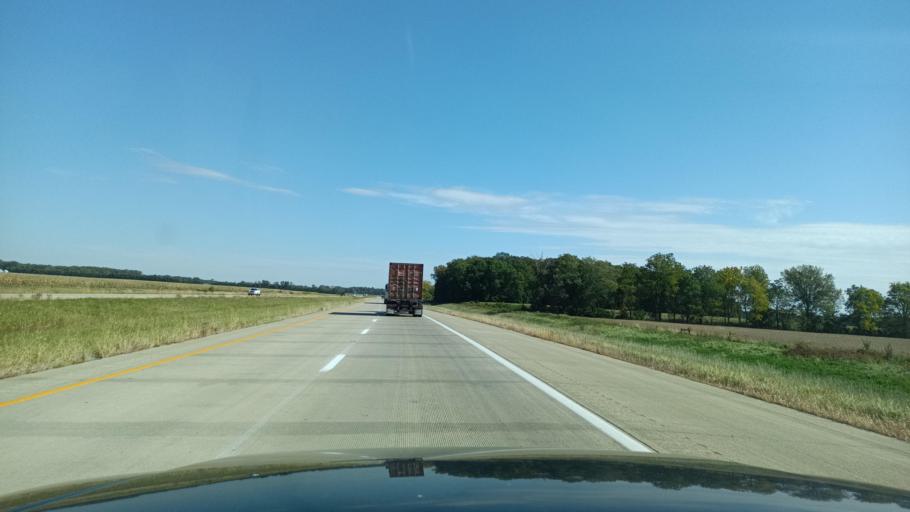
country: US
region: Ohio
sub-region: Henry County
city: Liberty Center
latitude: 41.4296
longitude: -83.9051
